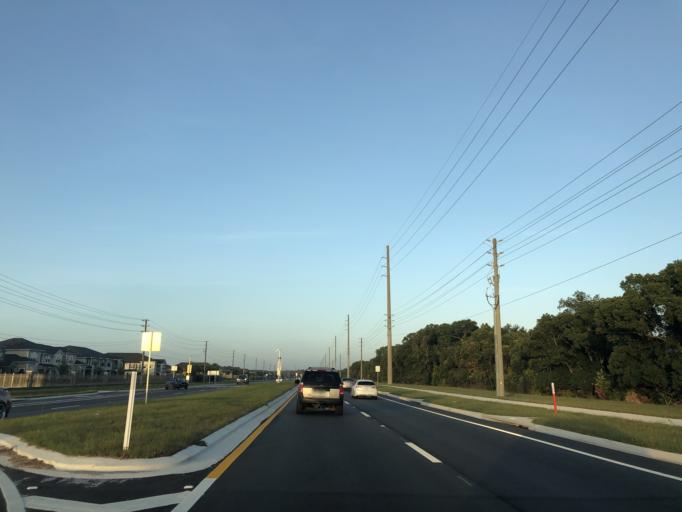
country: US
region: Florida
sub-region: Osceola County
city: Kissimmee
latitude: 28.3248
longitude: -81.4283
